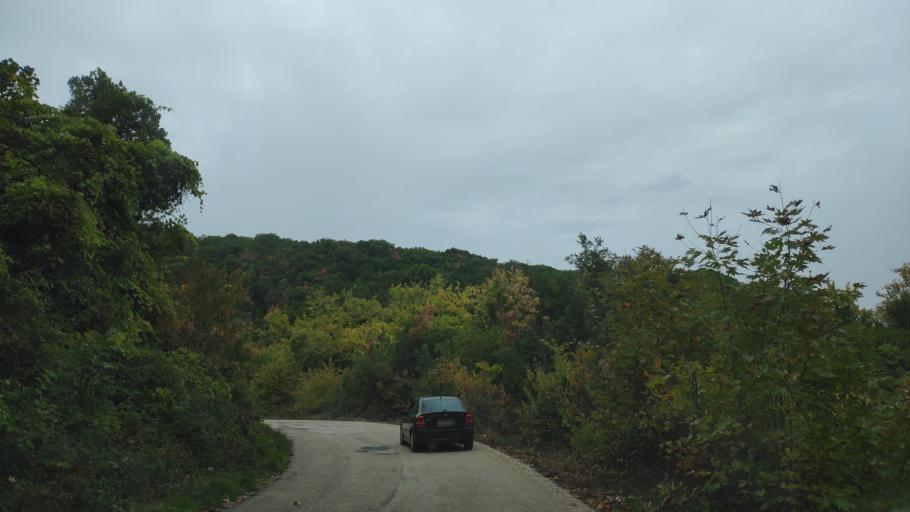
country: GR
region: Epirus
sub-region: Nomos Thesprotias
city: Paramythia
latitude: 39.4677
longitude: 20.6715
